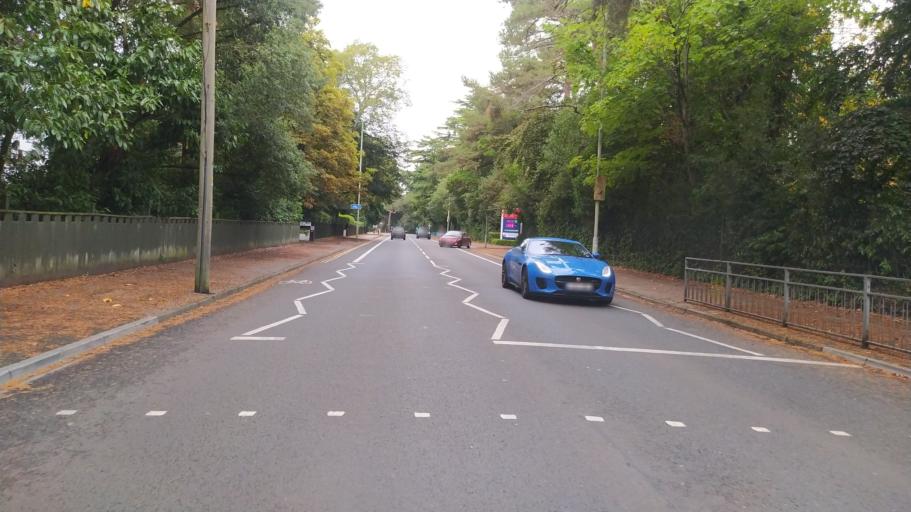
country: GB
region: England
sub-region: Dorset
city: Parkstone
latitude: 50.7246
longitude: -1.9145
